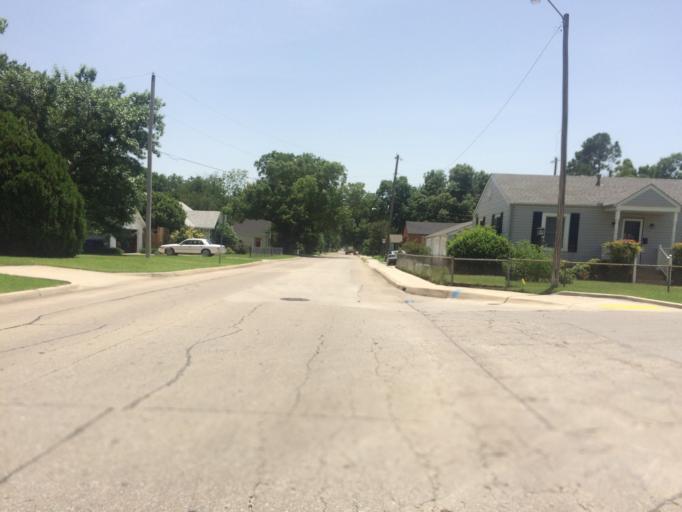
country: US
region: Oklahoma
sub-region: Cleveland County
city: Norman
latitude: 35.2176
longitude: -97.4547
